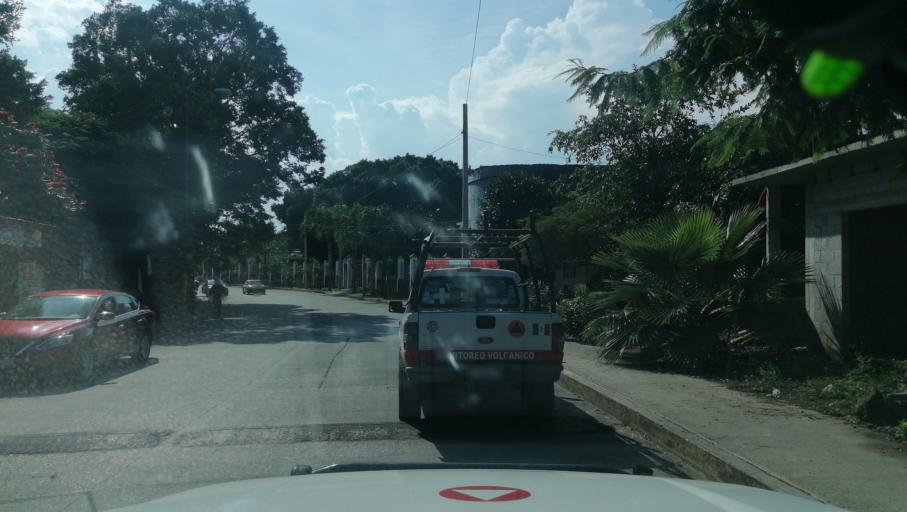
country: MX
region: Morelos
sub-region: Cuautla
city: Tierra Larga (Campo Nuevo)
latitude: 18.8391
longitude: -98.9452
